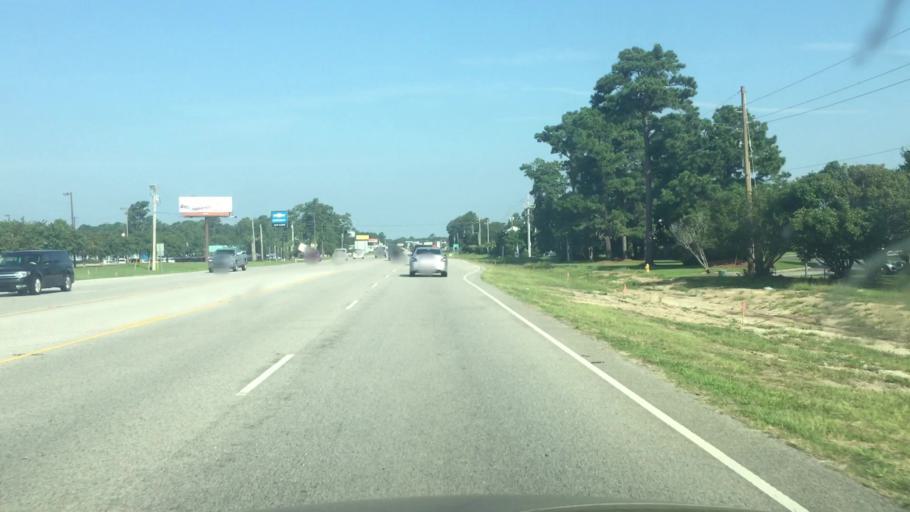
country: US
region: South Carolina
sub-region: Horry County
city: Little River
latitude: 33.8670
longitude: -78.6636
